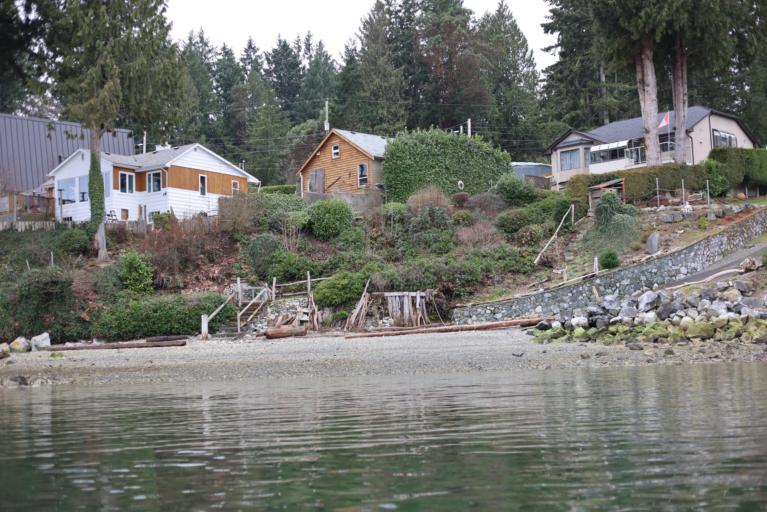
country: CA
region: British Columbia
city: North Saanich
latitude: 48.6396
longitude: -123.5396
